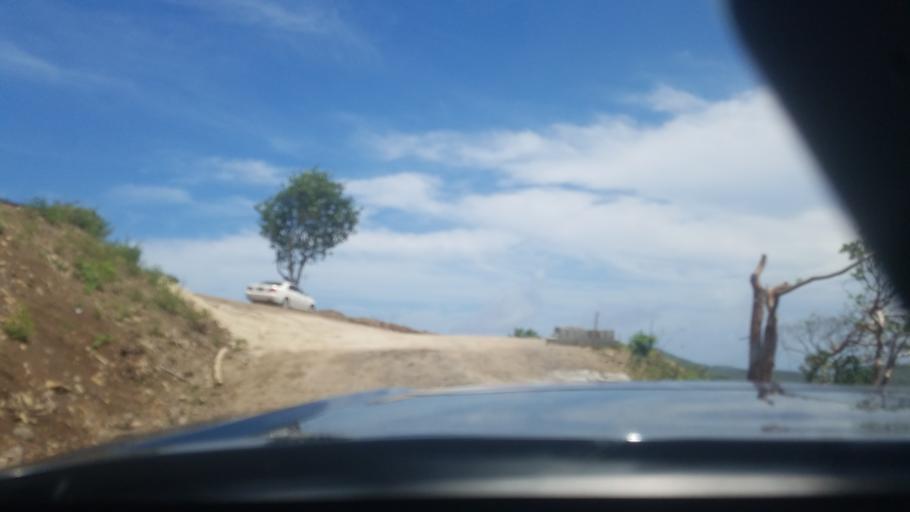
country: LC
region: Laborie Quarter
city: Laborie
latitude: 13.7417
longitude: -60.9667
